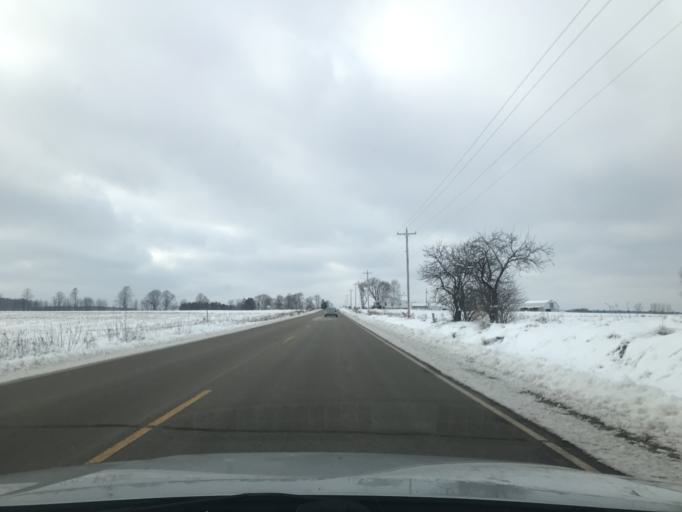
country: US
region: Wisconsin
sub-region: Oconto County
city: Oconto
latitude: 44.9499
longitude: -87.9091
